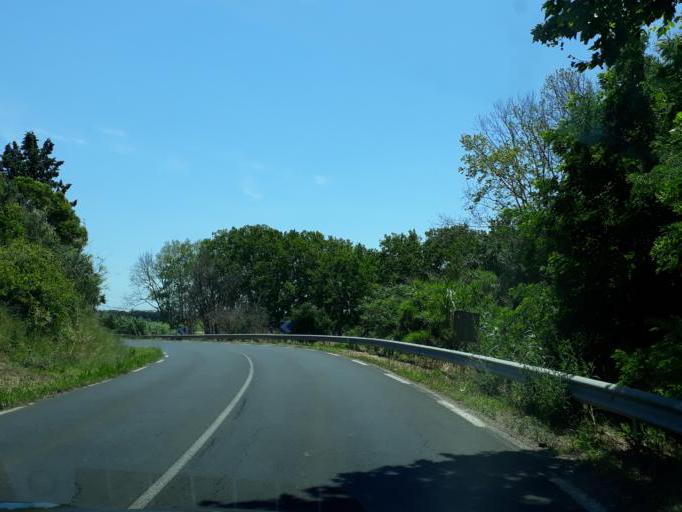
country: FR
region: Languedoc-Roussillon
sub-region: Departement de l'Herault
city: Sauvian
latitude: 43.3251
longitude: 3.2465
